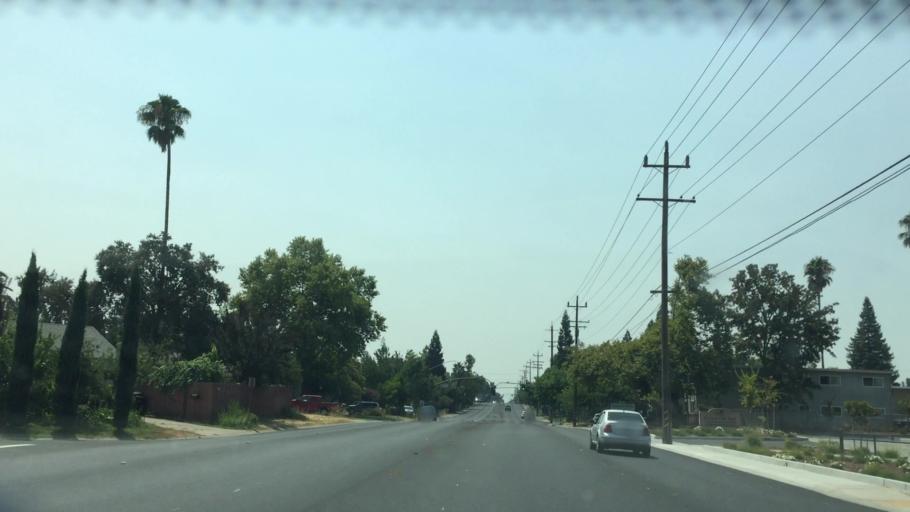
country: US
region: California
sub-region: Sacramento County
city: Arden-Arcade
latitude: 38.6228
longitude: -121.3645
